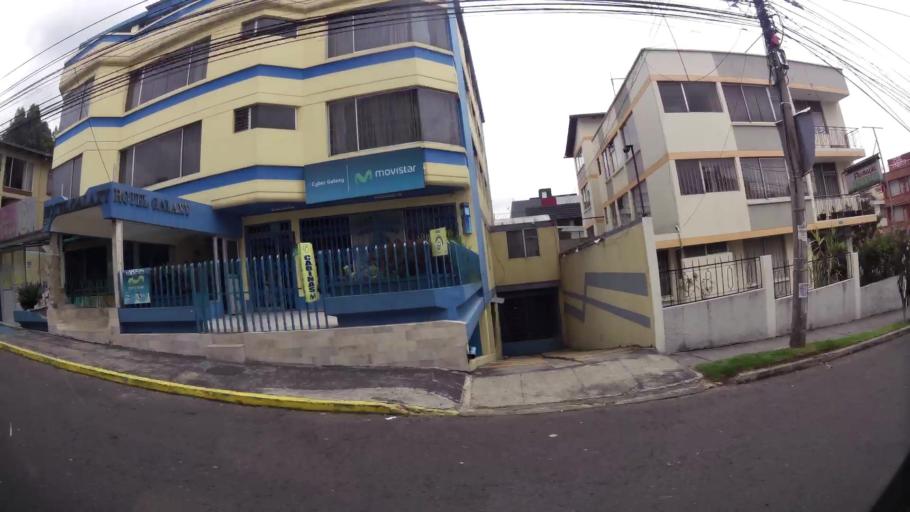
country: EC
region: Pichincha
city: Quito
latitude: -0.1724
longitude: -78.4928
